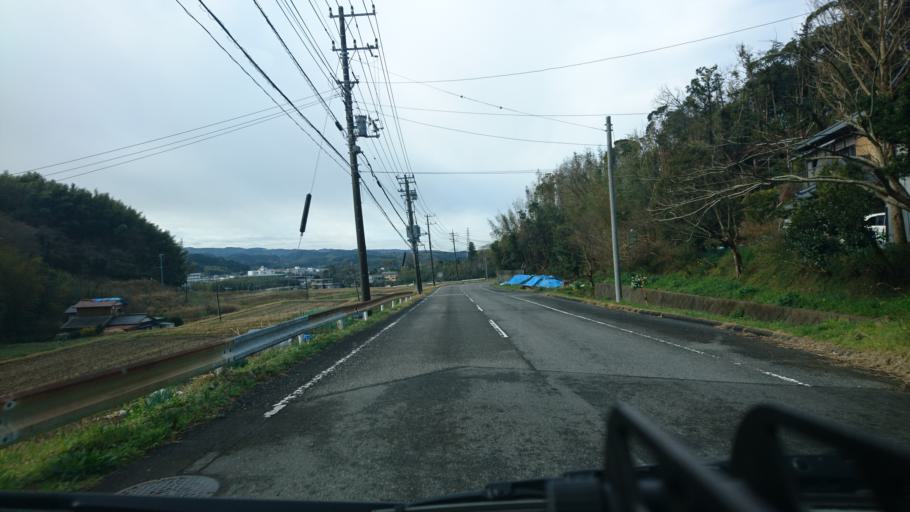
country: JP
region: Chiba
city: Kisarazu
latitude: 35.3153
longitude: 139.9636
